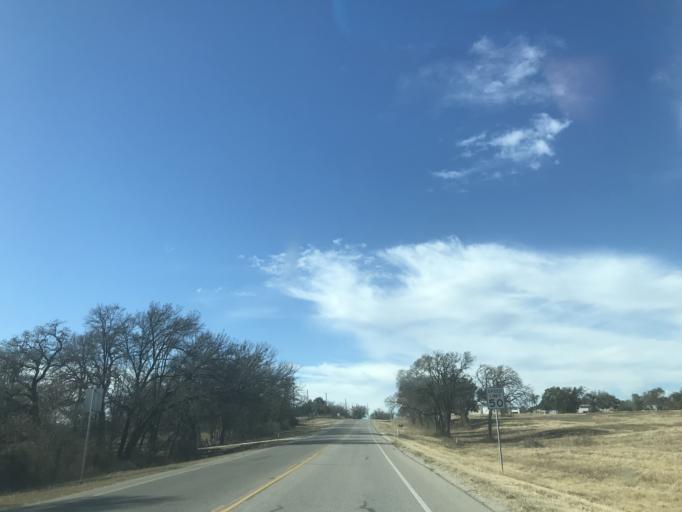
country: US
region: Texas
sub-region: Erath County
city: Stephenville
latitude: 32.2063
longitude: -98.1900
